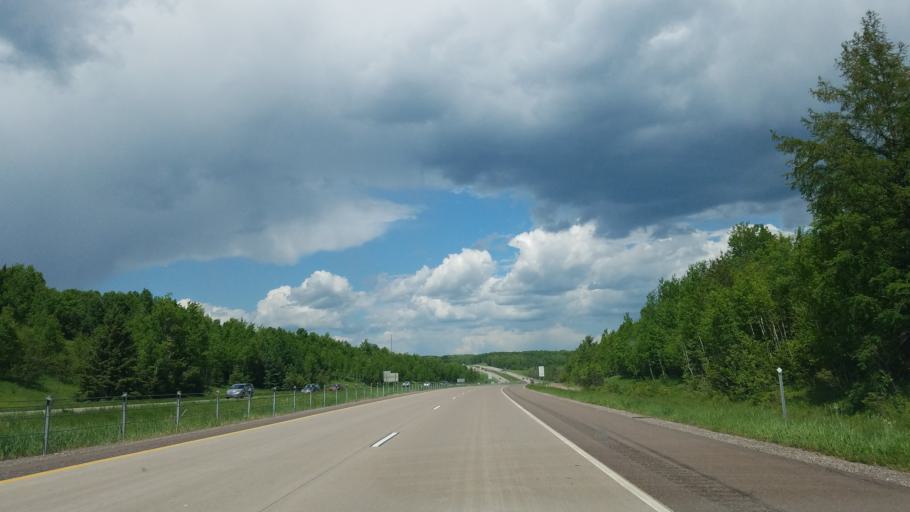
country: US
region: Minnesota
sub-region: Carlton County
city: Moose Lake
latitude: 46.4443
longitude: -92.7394
